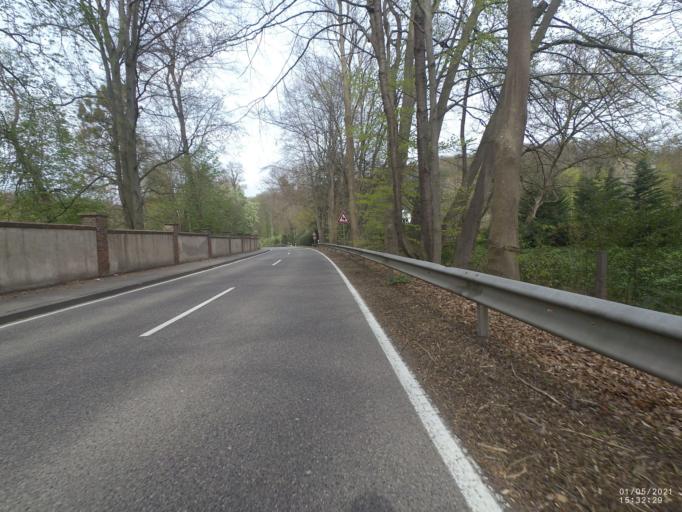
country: DE
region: Rheinland-Pfalz
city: Bassenheim
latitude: 50.3606
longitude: 7.4661
